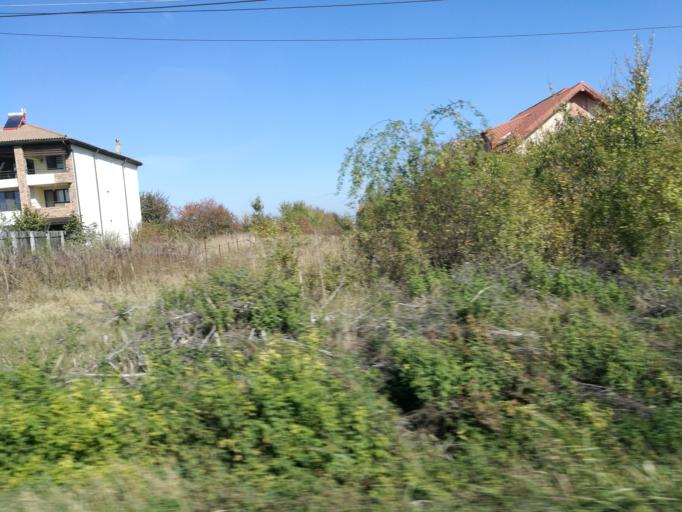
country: RO
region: Ilfov
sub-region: Comuna Dragomiresti-Vale
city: Dragomiresti-Vale
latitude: 44.4677
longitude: 25.9235
